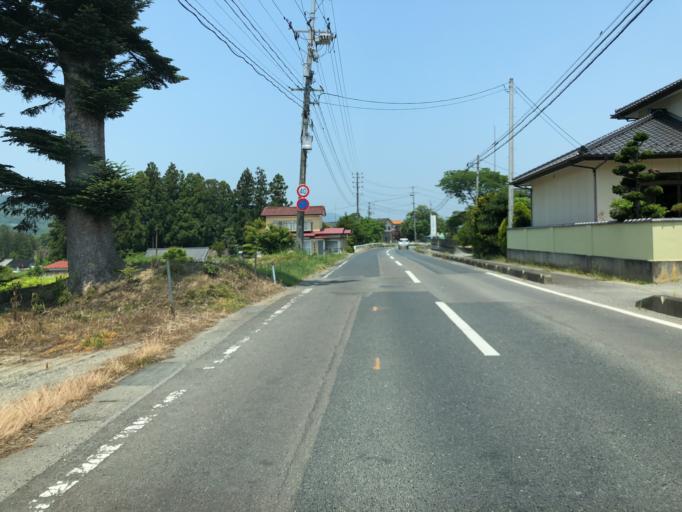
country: JP
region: Miyagi
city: Marumori
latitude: 37.8230
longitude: 140.8952
